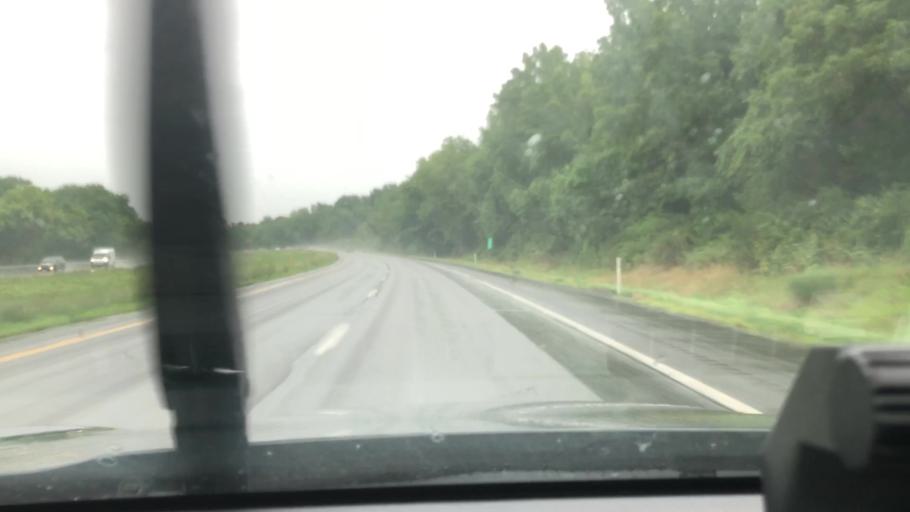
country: US
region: Pennsylvania
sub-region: Northampton County
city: Wind Gap
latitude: 40.8126
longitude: -75.3011
